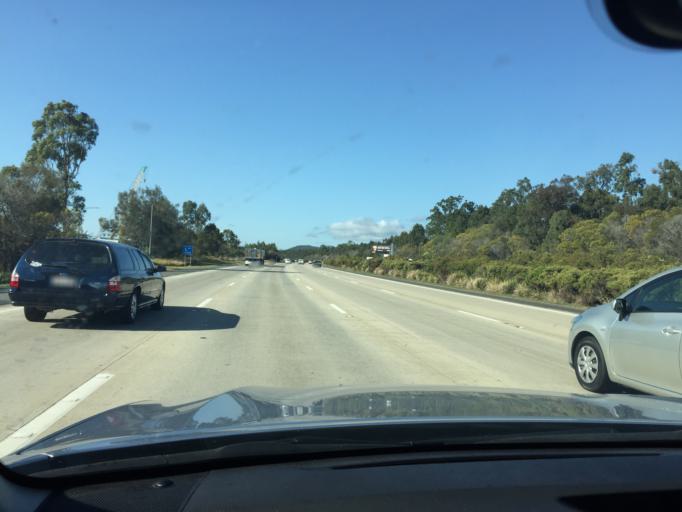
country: AU
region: Queensland
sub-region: Gold Coast
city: Ormeau Hills
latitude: -27.7725
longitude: 153.2518
